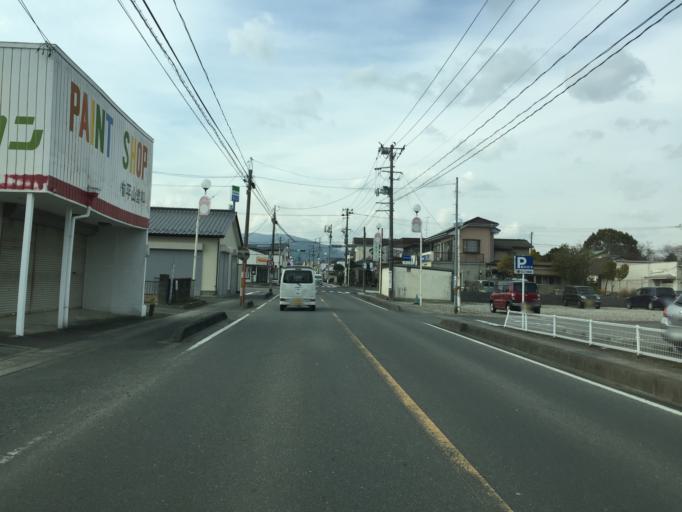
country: JP
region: Ibaraki
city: Kitaibaraki
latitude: 36.8898
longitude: 140.7668
